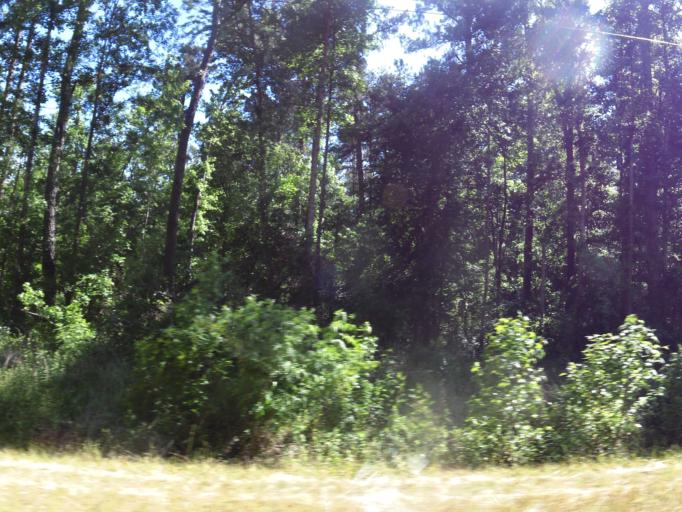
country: US
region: South Carolina
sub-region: Barnwell County
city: Blackville
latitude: 33.3441
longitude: -81.2440
